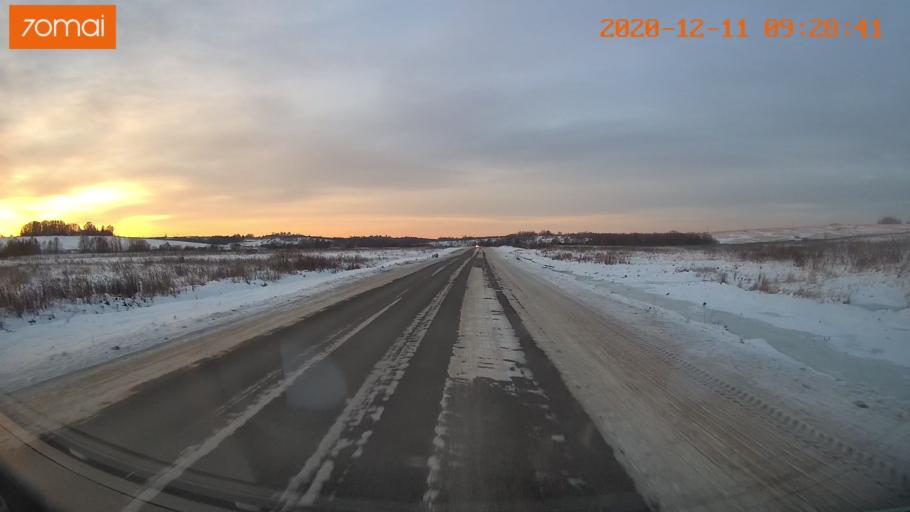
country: RU
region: Vologda
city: Vologda
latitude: 59.1503
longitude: 40.0067
